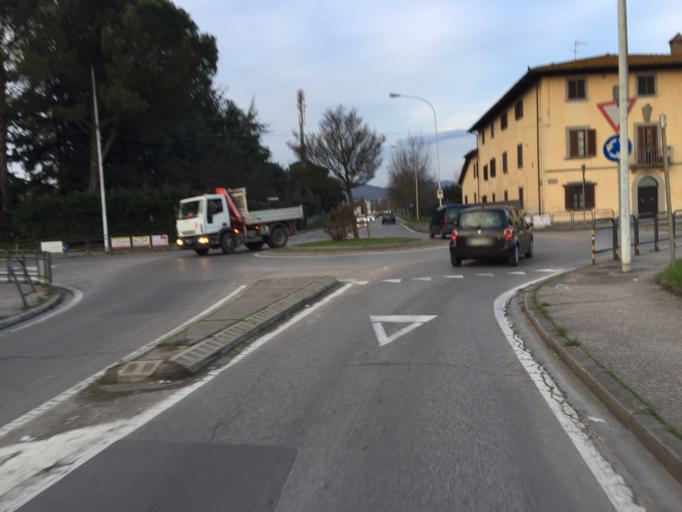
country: IT
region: Tuscany
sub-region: Provincia di Prato
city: Prato
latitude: 43.8846
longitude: 11.0601
